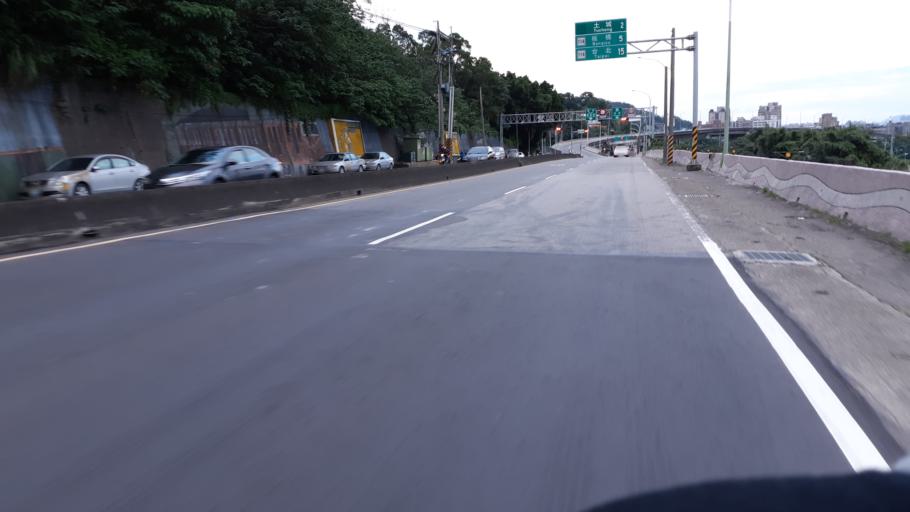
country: TW
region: Taiwan
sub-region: Taoyuan
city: Taoyuan
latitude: 24.9669
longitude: 121.3838
